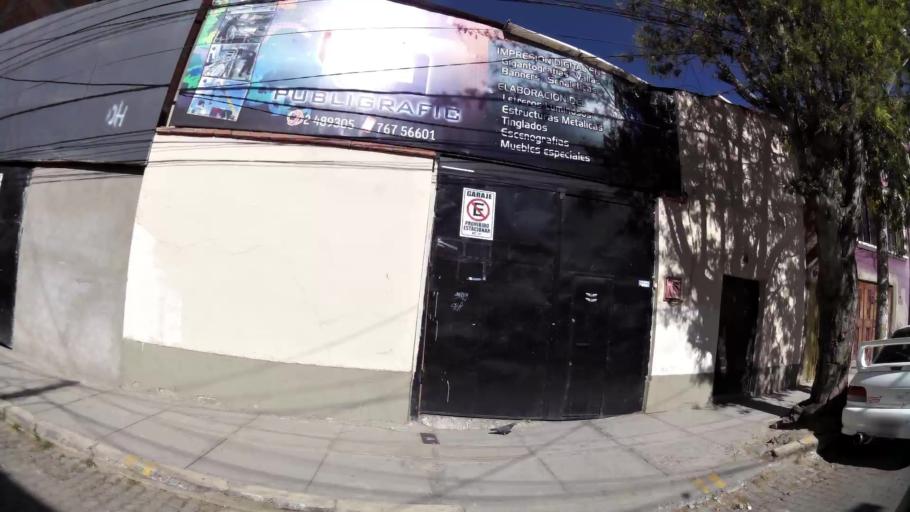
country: BO
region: La Paz
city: La Paz
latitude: -16.5075
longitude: -68.1344
